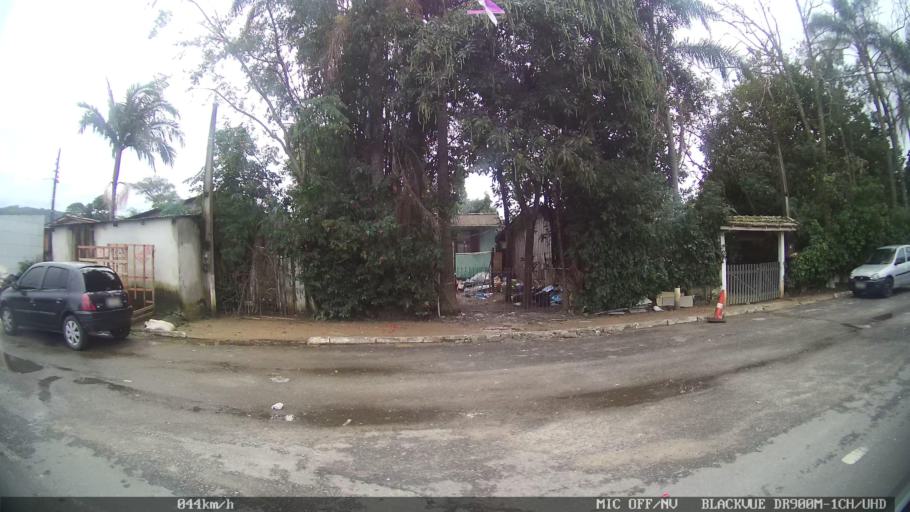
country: BR
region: Santa Catarina
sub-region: Biguacu
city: Biguacu
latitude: -27.5382
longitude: -48.6397
